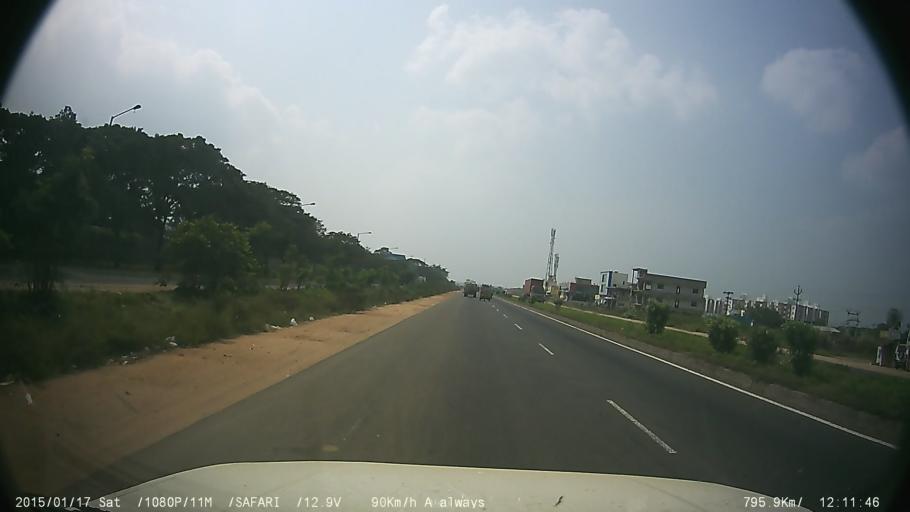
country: IN
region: Tamil Nadu
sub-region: Kancheepuram
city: Sriperumbudur
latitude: 12.9364
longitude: 79.9117
